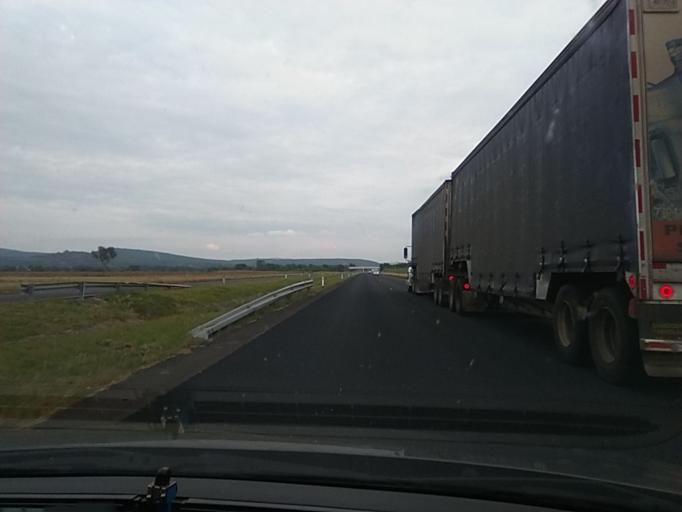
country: MX
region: Michoacan
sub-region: Jimenez
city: Copandaro (Copandaro del Cuatro)
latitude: 19.9203
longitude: -101.5967
